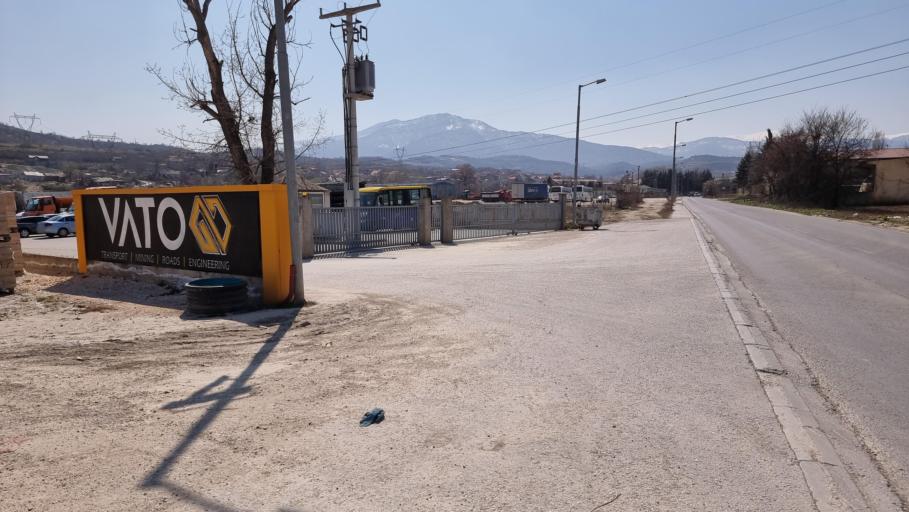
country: MK
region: Kisela Voda
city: Kisela Voda
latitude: 41.9350
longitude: 21.4990
